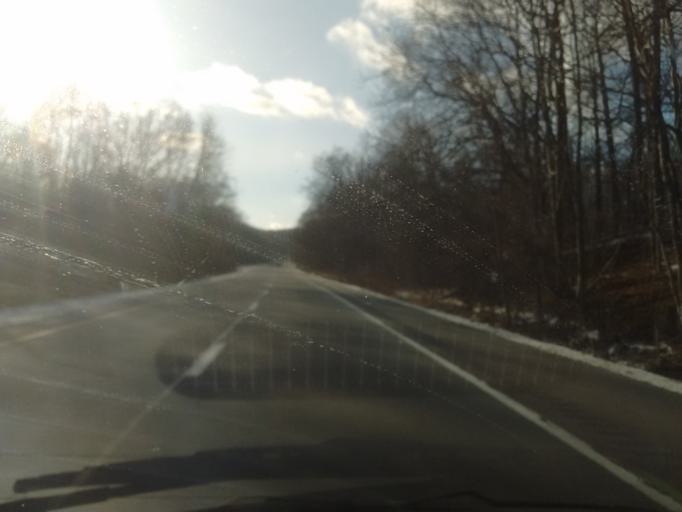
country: US
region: New York
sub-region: Dutchess County
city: Brinckerhoff
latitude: 41.5280
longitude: -73.8538
